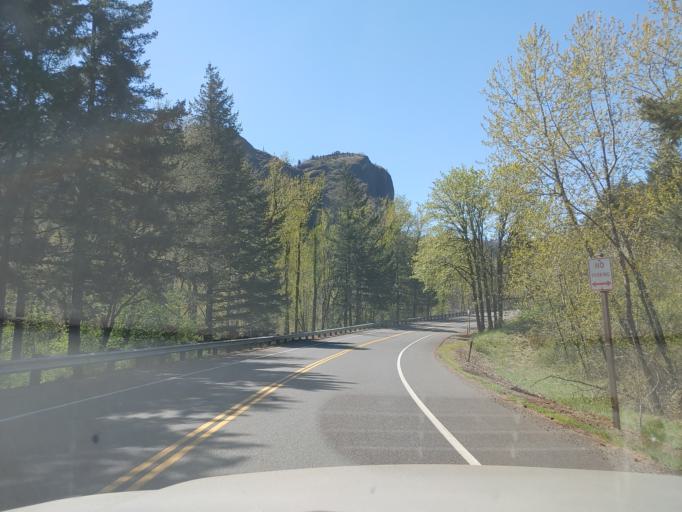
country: US
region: Washington
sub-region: Clark County
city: Washougal
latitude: 45.5434
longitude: -122.2369
